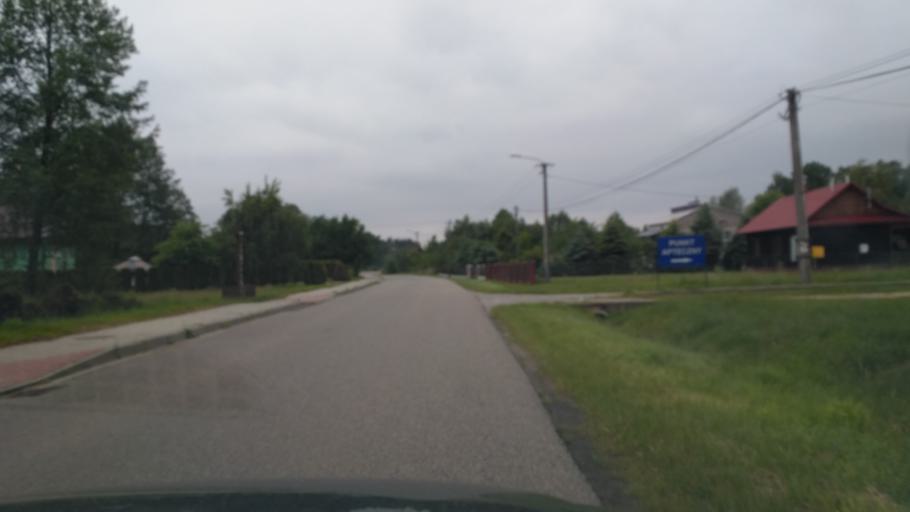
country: PL
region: Subcarpathian Voivodeship
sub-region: Powiat kolbuszowski
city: Niwiska
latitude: 50.1504
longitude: 21.6702
